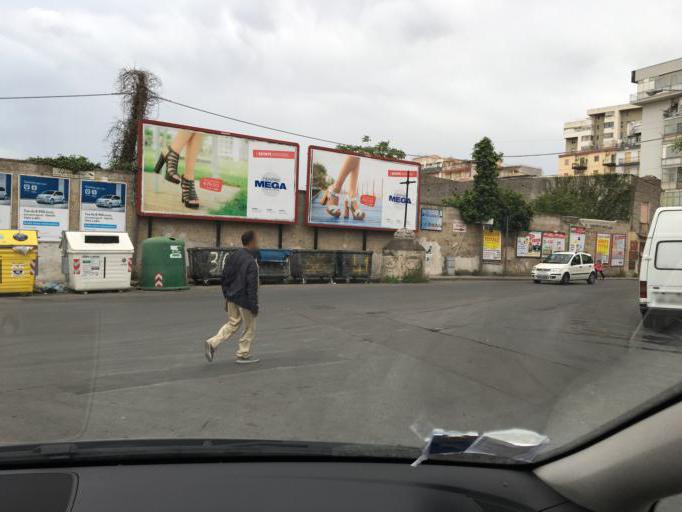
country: IT
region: Sicily
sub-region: Palermo
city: Palermo
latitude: 38.1115
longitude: 13.3394
